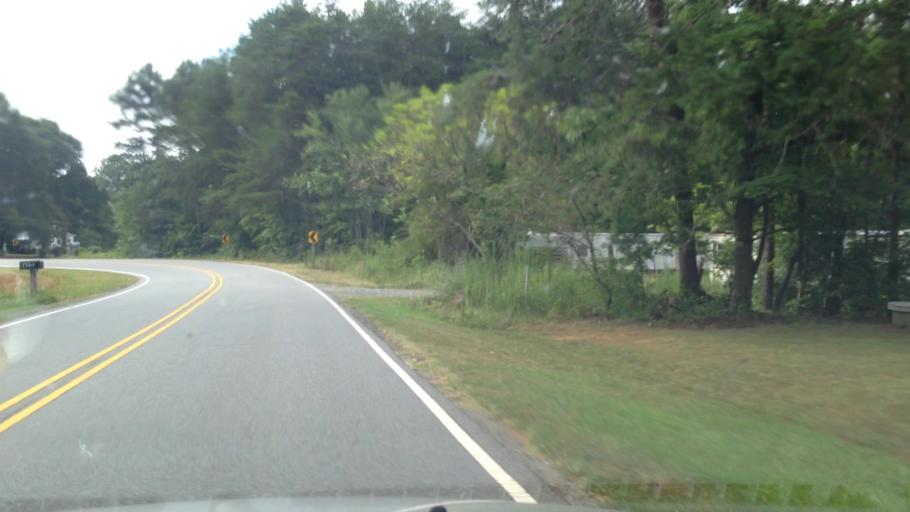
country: US
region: North Carolina
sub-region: Rockingham County
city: Mayodan
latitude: 36.4015
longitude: -80.0416
